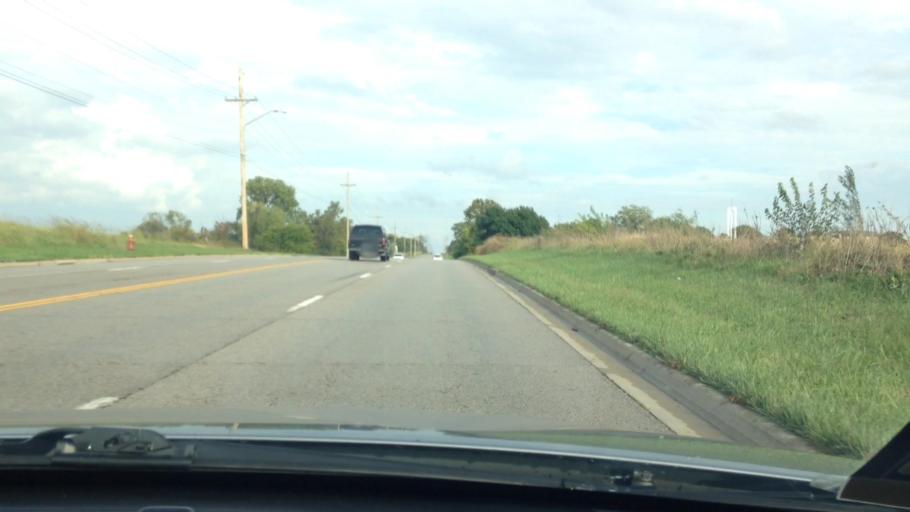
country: US
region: Kansas
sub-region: Leavenworth County
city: Basehor
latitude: 39.1286
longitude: -94.8799
